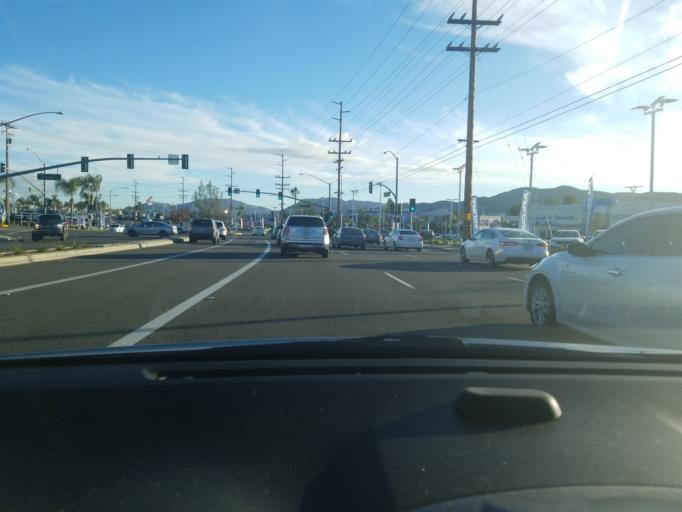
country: US
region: California
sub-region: Riverside County
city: Temecula
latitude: 33.5151
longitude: -117.1554
